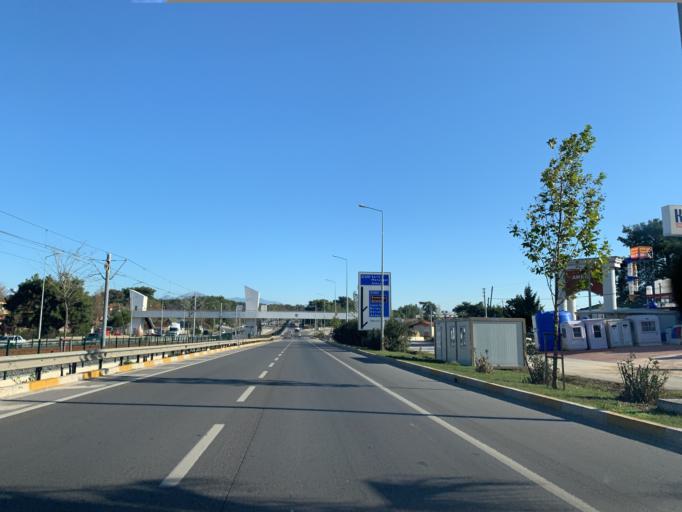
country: TR
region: Antalya
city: Aksu
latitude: 36.9419
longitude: 30.8257
